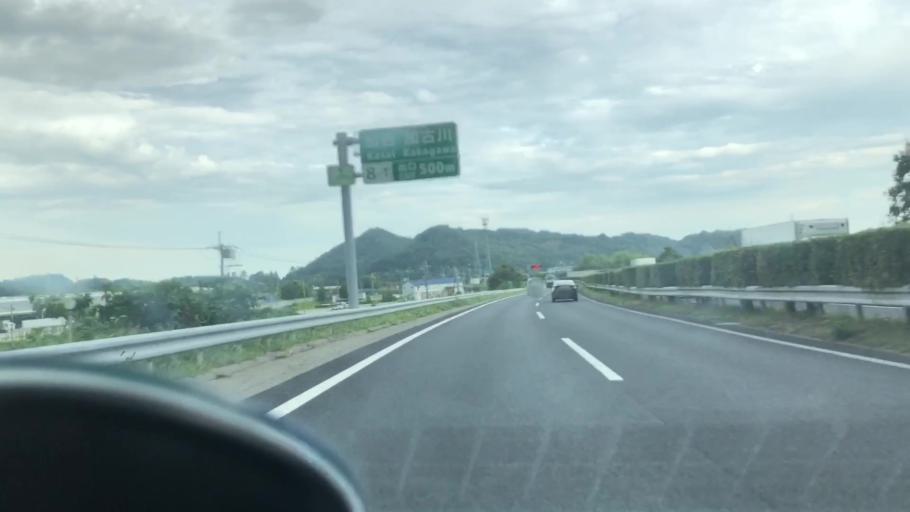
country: JP
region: Hyogo
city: Yashiro
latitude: 34.9365
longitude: 134.8580
